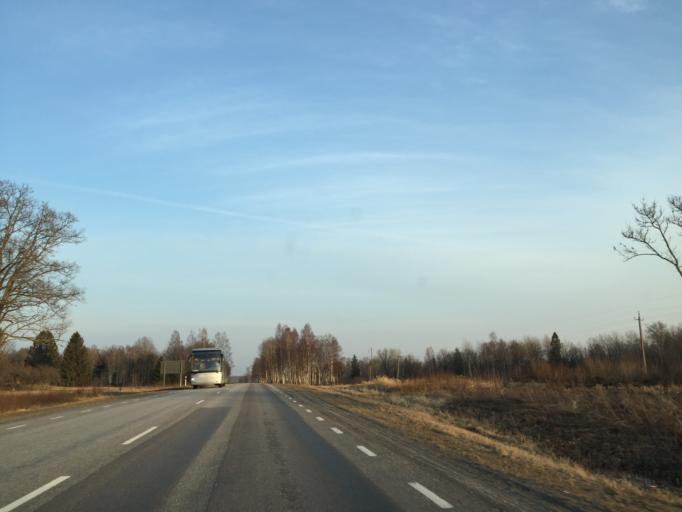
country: EE
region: Laeaene
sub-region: Lihula vald
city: Lihula
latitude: 58.5440
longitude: 24.0016
